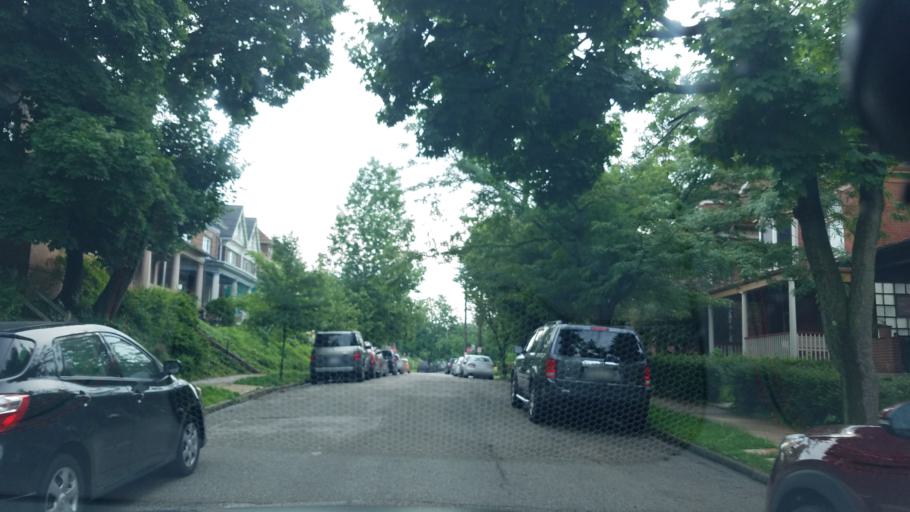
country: US
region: Pennsylvania
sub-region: Allegheny County
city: Wilkinsburg
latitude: 40.4367
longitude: -79.8890
